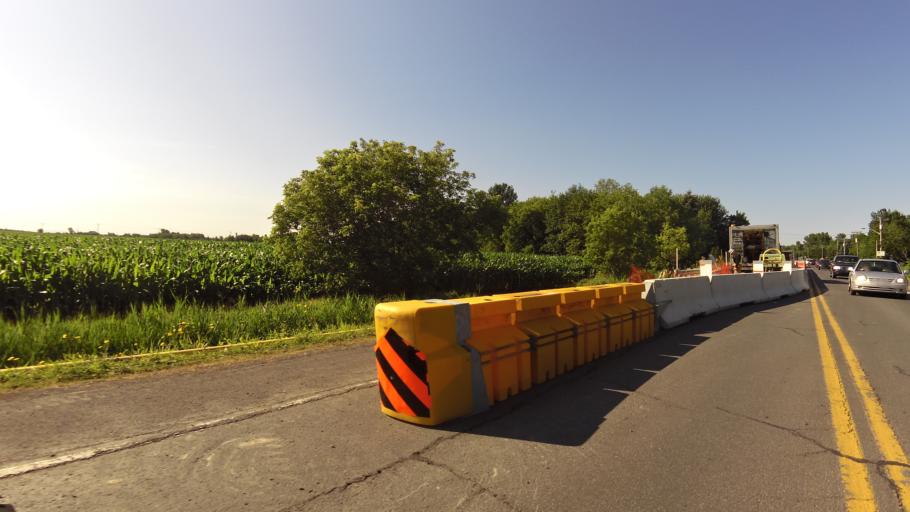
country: CA
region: Quebec
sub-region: Monteregie
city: Napierville
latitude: 45.2005
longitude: -73.3967
